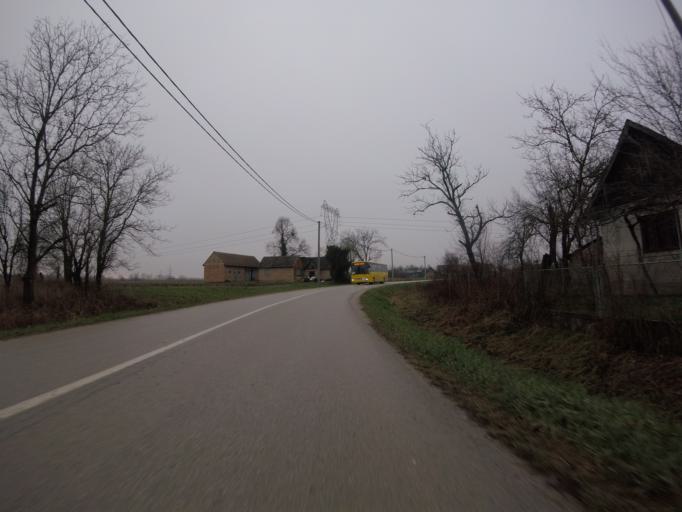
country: HR
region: Sisacko-Moslavacka
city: Lekenik
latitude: 45.6614
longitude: 16.2516
